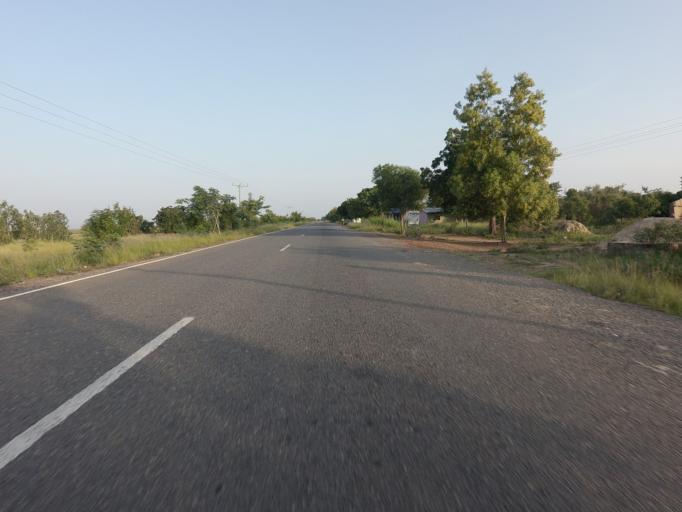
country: GH
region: Volta
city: Anloga
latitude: 5.9061
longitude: 0.7111
